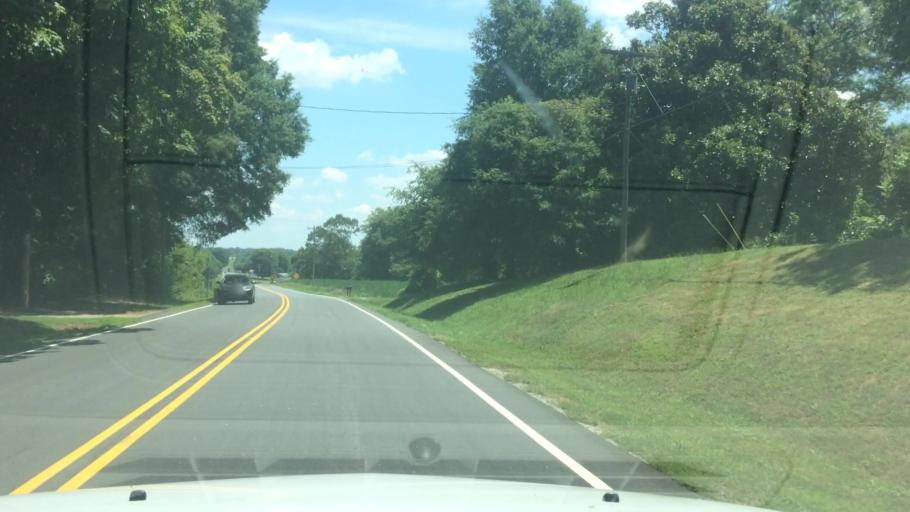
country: US
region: North Carolina
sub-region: Alexander County
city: Taylorsville
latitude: 35.9197
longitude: -81.2331
